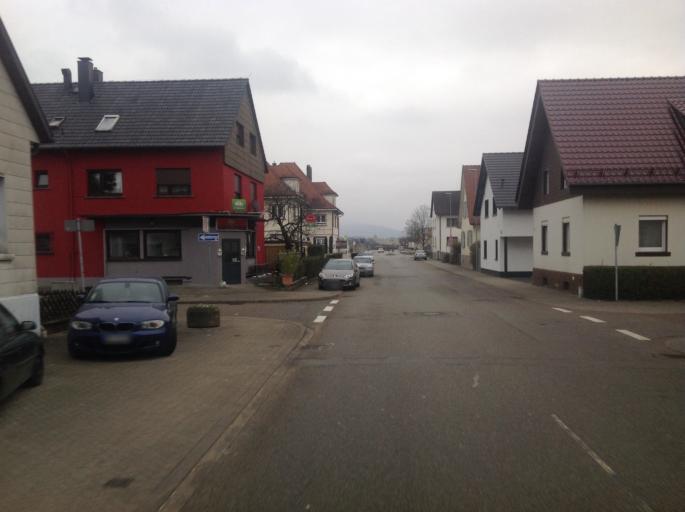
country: DE
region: Baden-Wuerttemberg
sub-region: Karlsruhe Region
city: Iffezheim
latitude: 48.8208
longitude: 8.1478
